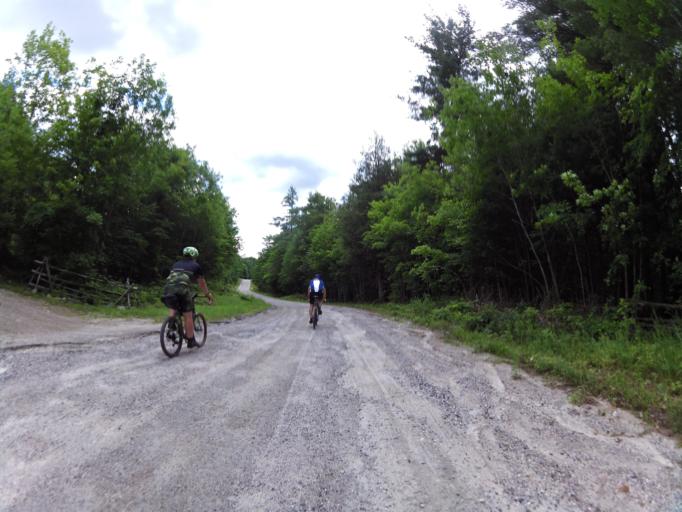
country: CA
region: Ontario
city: Perth
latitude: 45.0518
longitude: -76.4796
